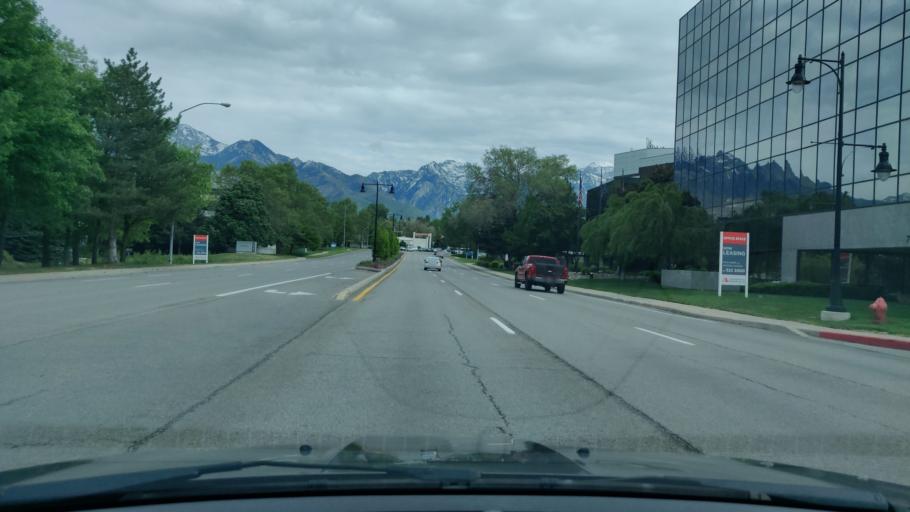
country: US
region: Utah
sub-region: Salt Lake County
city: Little Cottonwood Creek Valley
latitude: 40.6234
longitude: -111.8586
